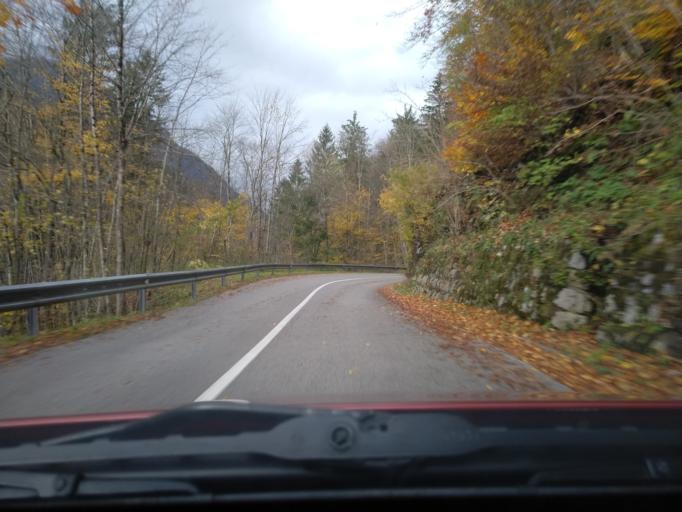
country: SI
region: Kamnik
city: Mekinje
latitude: 46.2970
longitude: 14.6129
